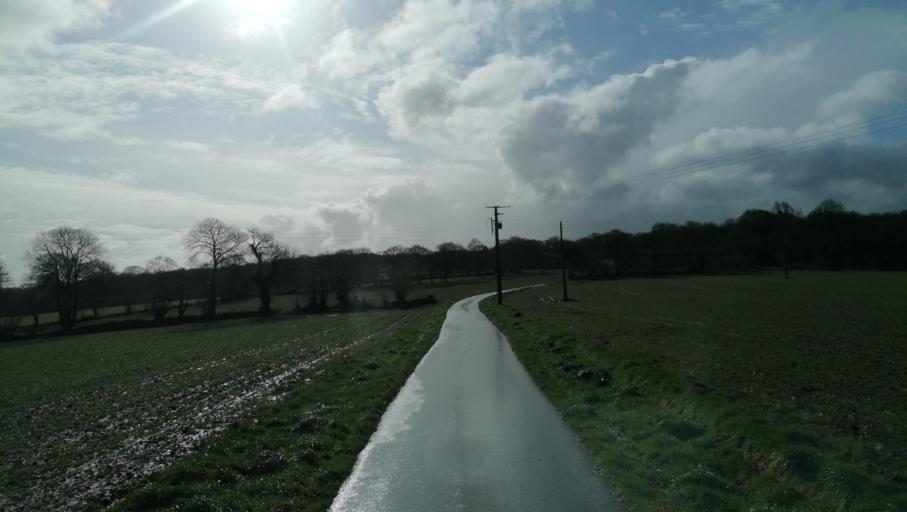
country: FR
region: Brittany
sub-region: Departement des Cotes-d'Armor
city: Lanrodec
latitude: 48.4853
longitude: -3.0206
